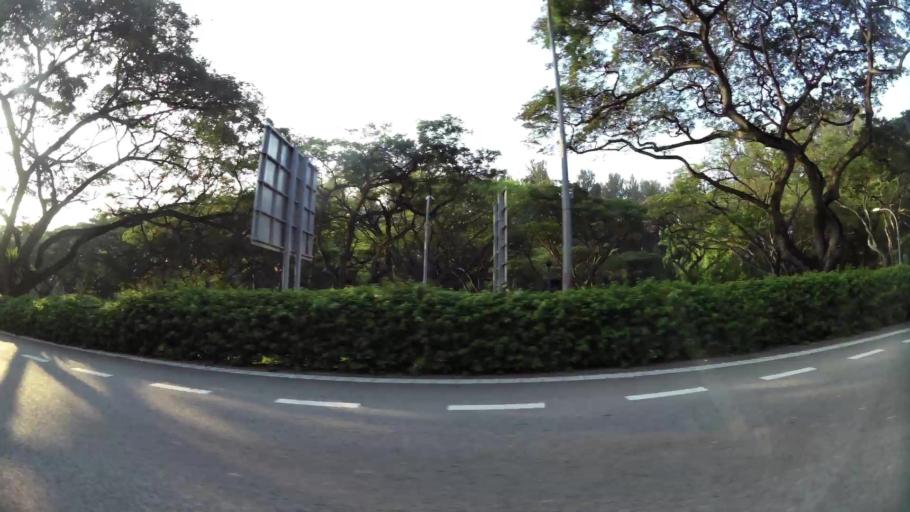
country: SG
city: Singapore
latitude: 1.2954
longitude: 103.8920
